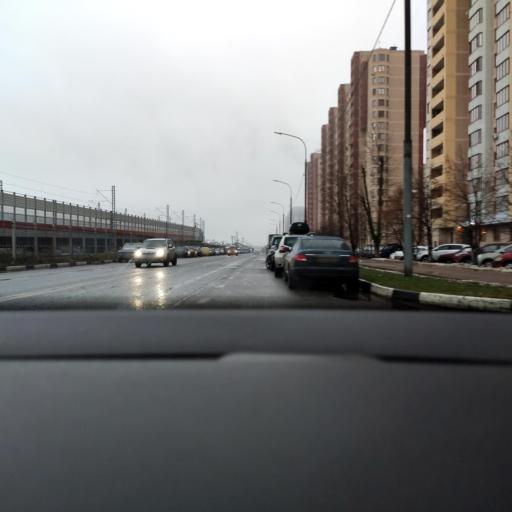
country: RU
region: Moskovskaya
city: Reutov
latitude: 55.7534
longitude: 37.8674
